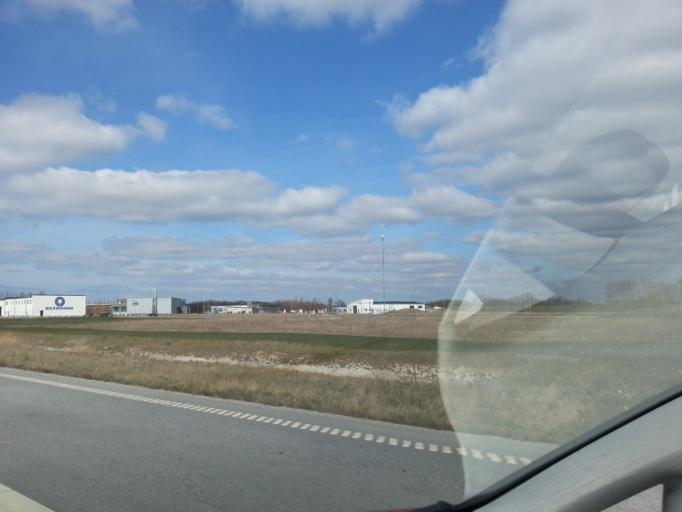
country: SE
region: Skane
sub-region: Vellinge Kommun
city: Vellinge
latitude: 55.4568
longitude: 13.0170
